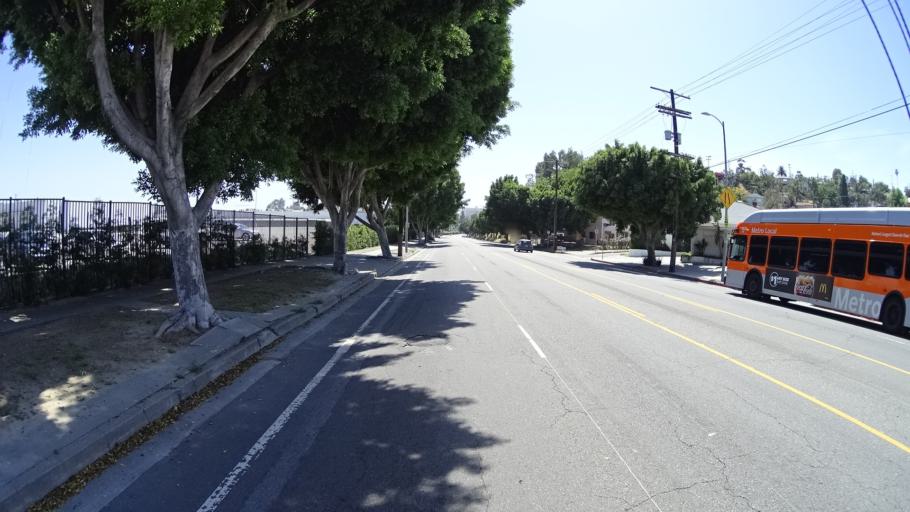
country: US
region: California
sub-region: Los Angeles County
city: Boyle Heights
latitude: 34.0732
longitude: -118.1968
